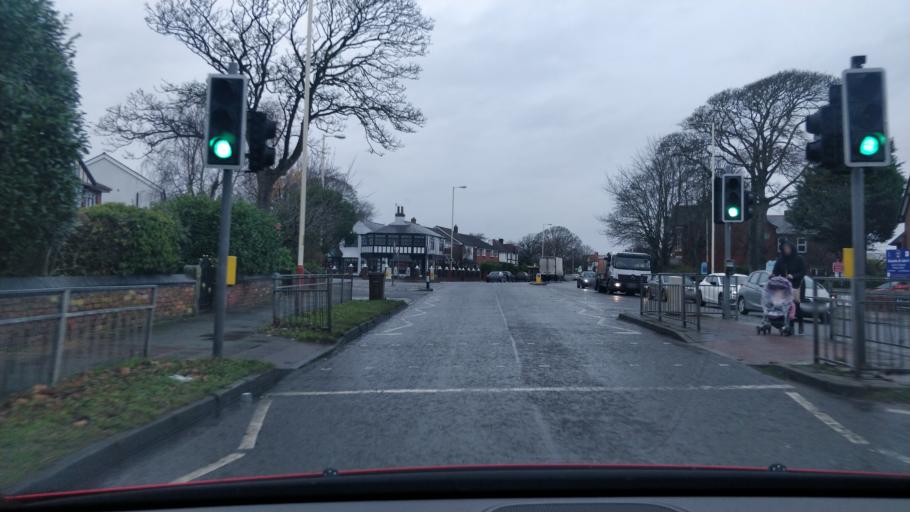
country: GB
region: England
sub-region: Sefton
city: Formby
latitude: 53.5987
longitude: -3.0349
